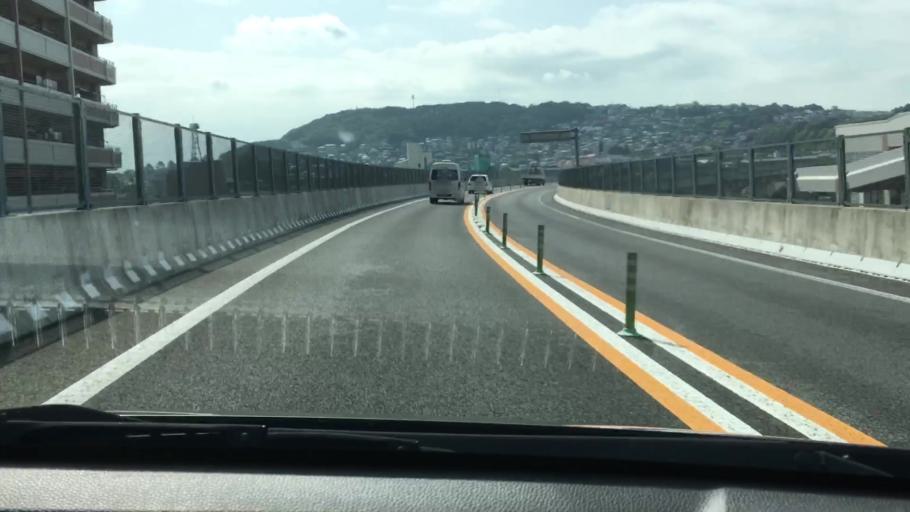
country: JP
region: Nagasaki
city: Sasebo
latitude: 33.1622
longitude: 129.7274
